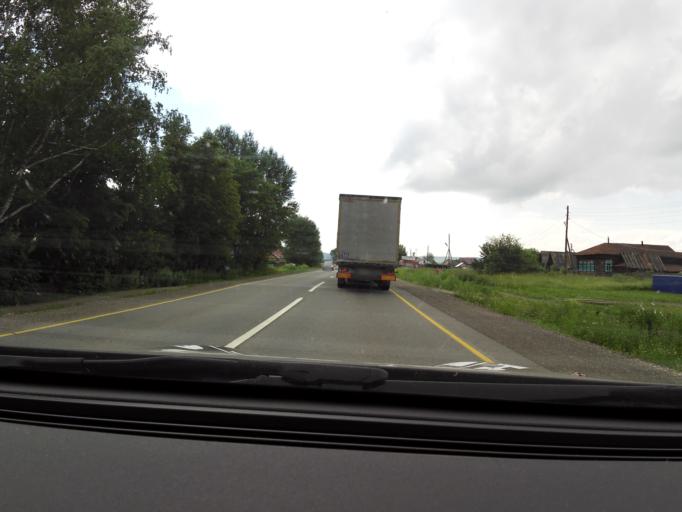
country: RU
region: Perm
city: Suksun
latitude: 57.0591
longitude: 57.4254
